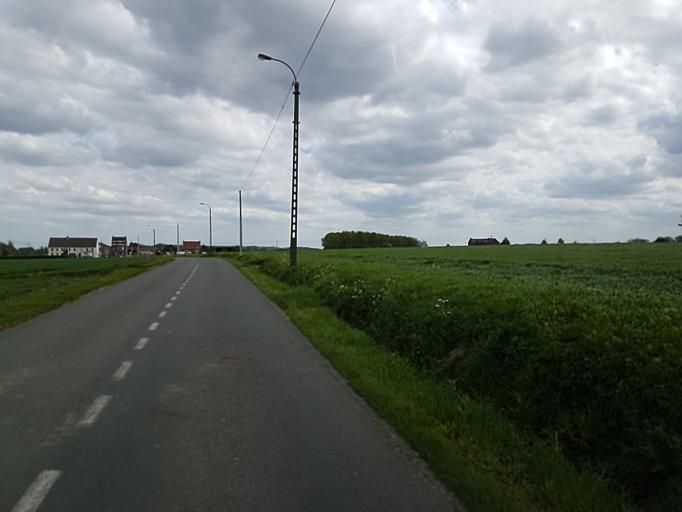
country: BE
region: Wallonia
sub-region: Province du Hainaut
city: Celles
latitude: 50.7033
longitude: 3.4760
